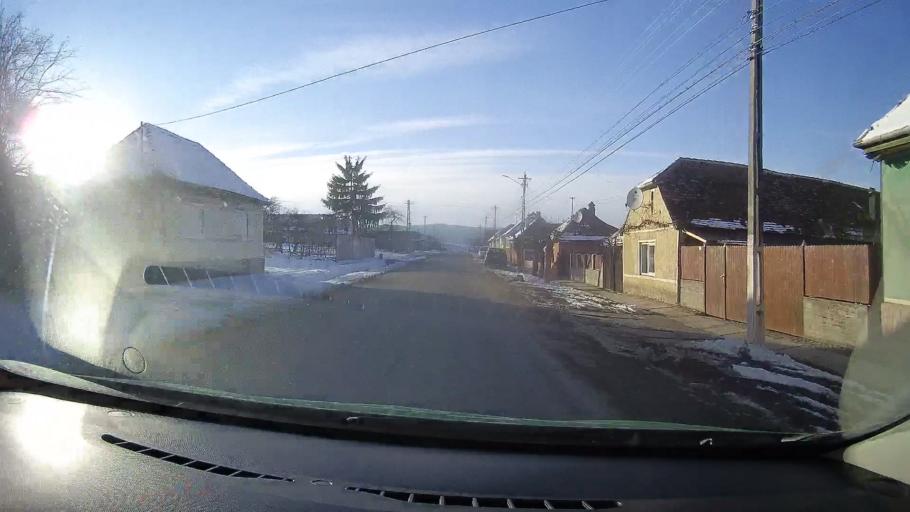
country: RO
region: Sibiu
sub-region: Comuna Merghindeal
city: Merghindeal
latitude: 45.9666
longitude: 24.7165
